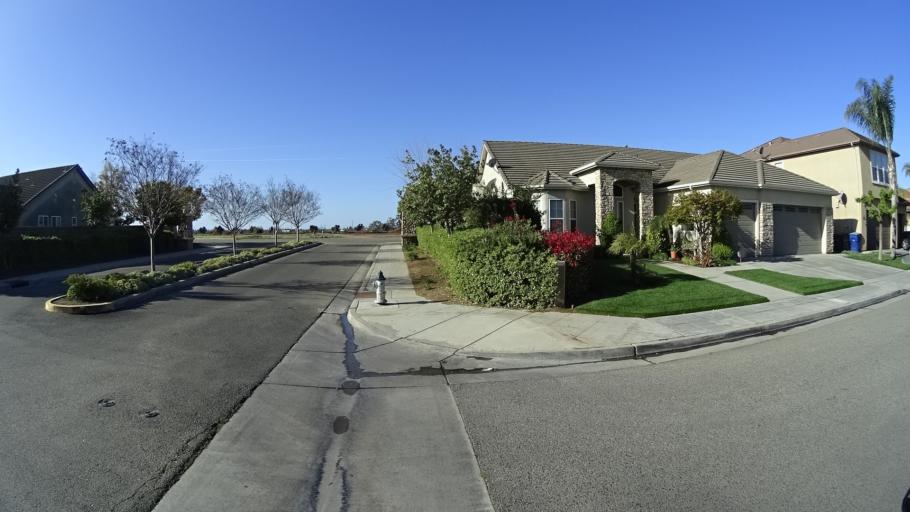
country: US
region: California
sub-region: Fresno County
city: Biola
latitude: 36.8305
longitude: -119.9034
